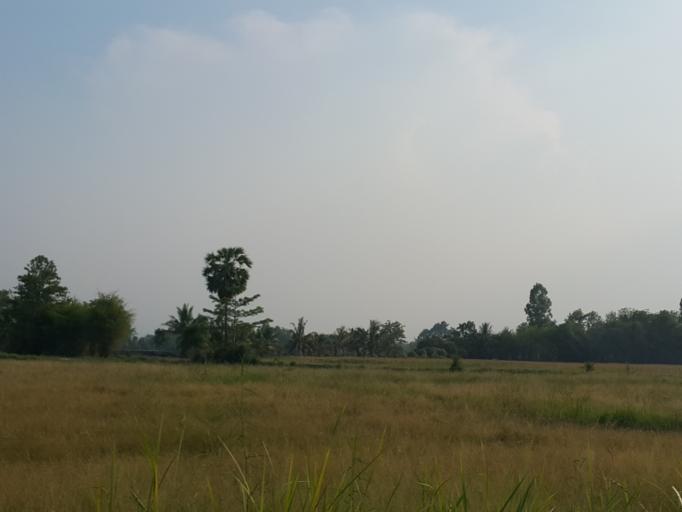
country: TH
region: Uthai Thani
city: Huai Khot
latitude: 15.3127
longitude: 99.6736
